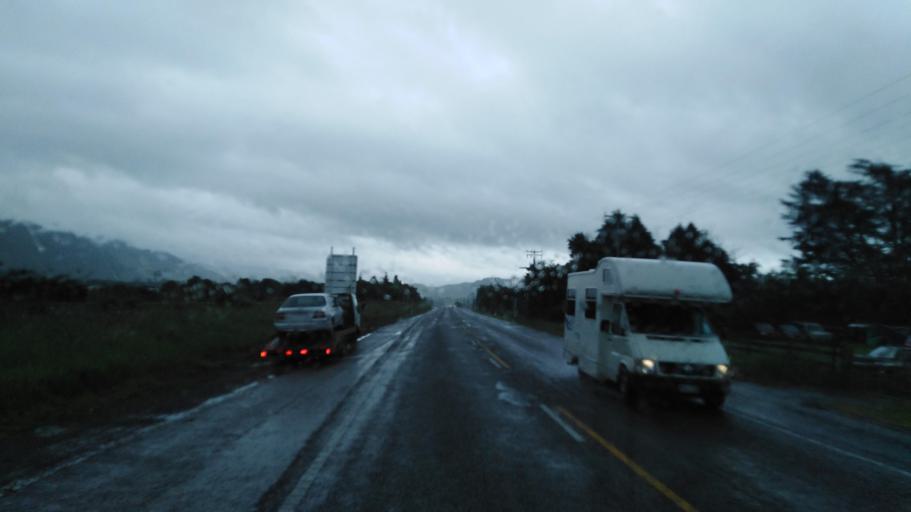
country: NZ
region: Manawatu-Wanganui
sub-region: Horowhenua District
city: Levin
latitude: -40.7019
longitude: 175.2221
